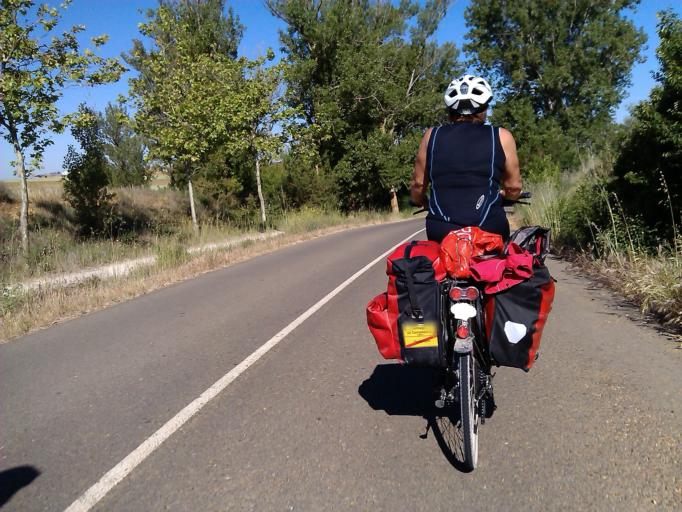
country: ES
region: Castille and Leon
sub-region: Provincia de Leon
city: Bercianos del Real Camino
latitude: 42.3890
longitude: -5.1301
